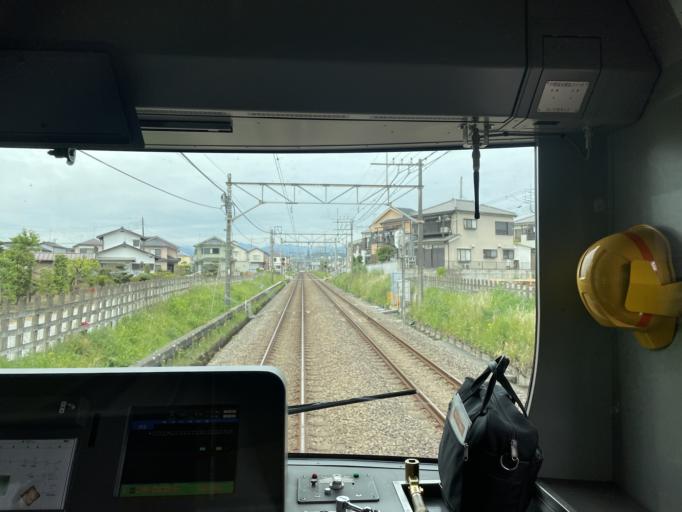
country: JP
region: Saitama
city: Hanno
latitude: 35.8426
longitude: 139.3379
